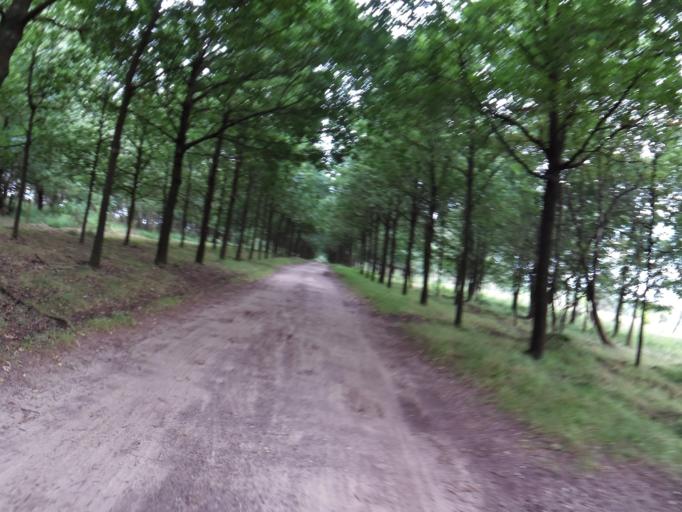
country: NL
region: Gelderland
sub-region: Gemeente Arnhem
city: Gulden Bodem
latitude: 52.0549
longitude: 5.9103
